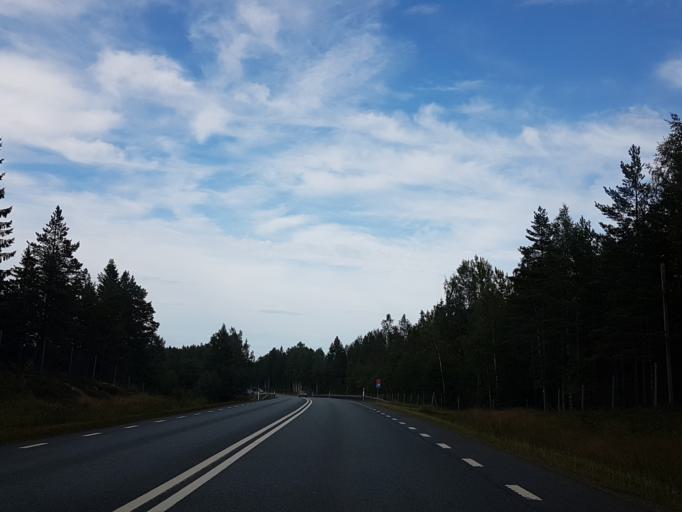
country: SE
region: Vaesterbotten
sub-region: Robertsfors Kommun
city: Robertsfors
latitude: 64.0170
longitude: 20.8310
